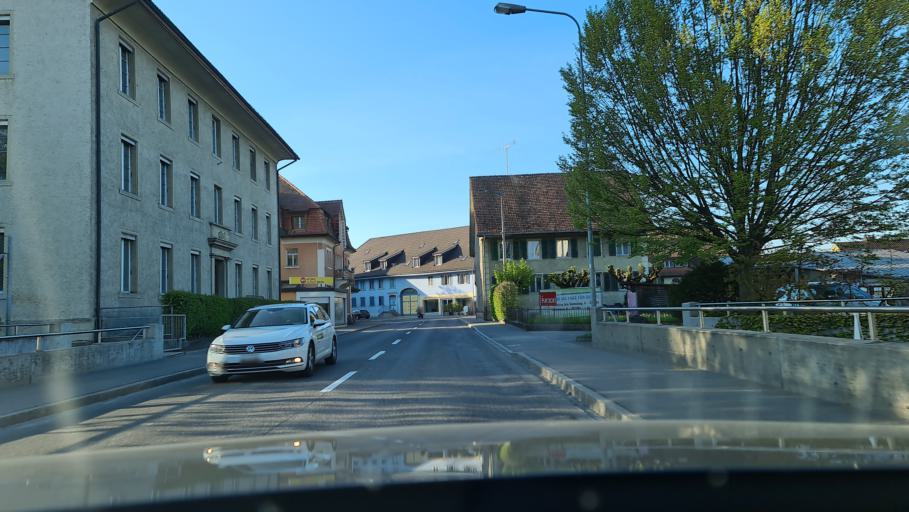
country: CH
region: Aargau
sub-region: Bezirk Lenzburg
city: Seon
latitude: 47.3446
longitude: 8.1603
